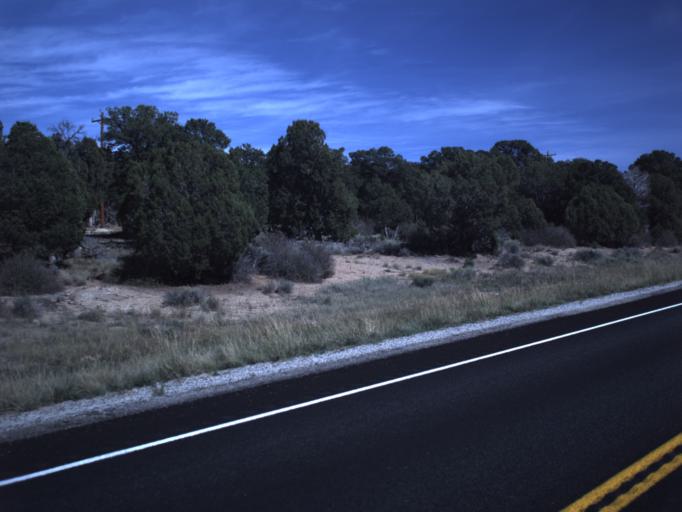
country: US
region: Utah
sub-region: San Juan County
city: Monticello
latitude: 37.8419
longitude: -109.1307
